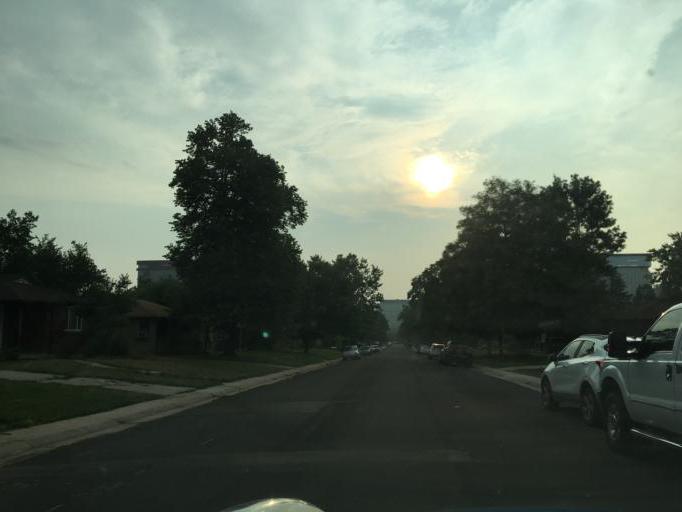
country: US
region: Colorado
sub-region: Arapahoe County
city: Glendale
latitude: 39.6843
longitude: -104.9326
